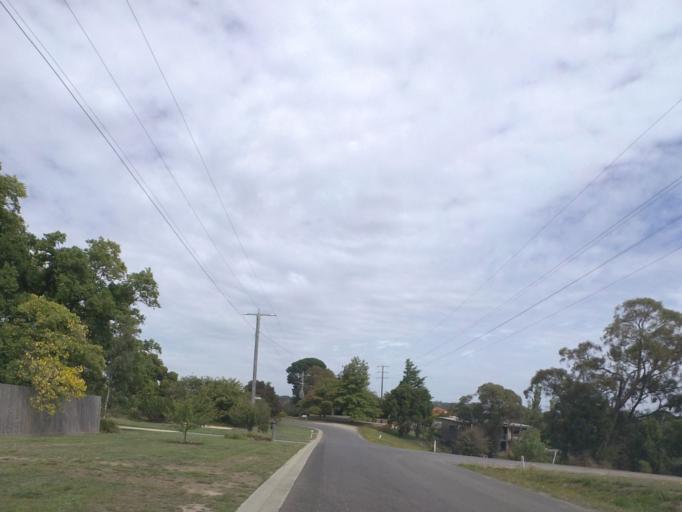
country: AU
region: Victoria
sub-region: Hume
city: Sunbury
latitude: -37.3548
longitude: 144.5358
